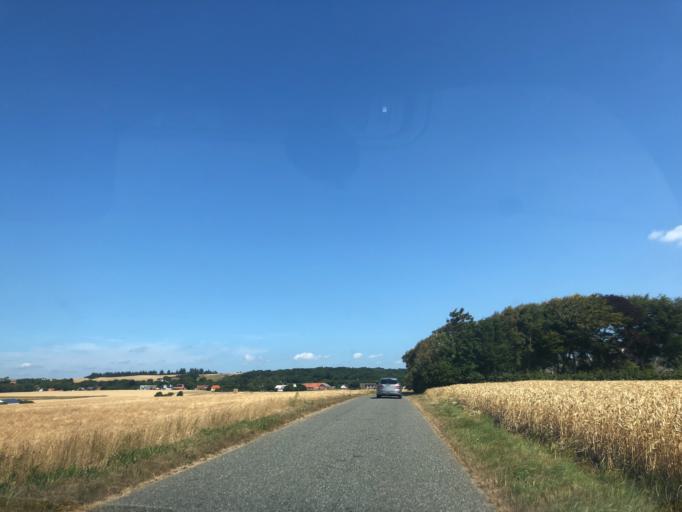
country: DK
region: North Denmark
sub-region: Morso Kommune
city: Nykobing Mors
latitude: 56.8149
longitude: 8.9963
